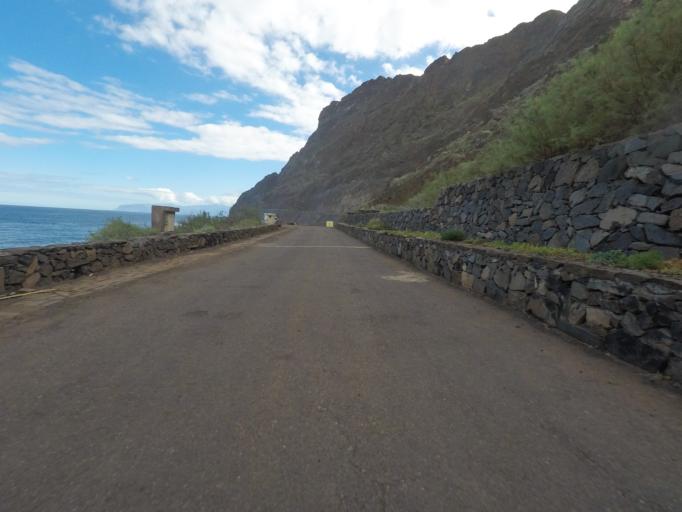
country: ES
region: Canary Islands
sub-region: Provincia de Santa Cruz de Tenerife
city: Hermigua
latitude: 28.1772
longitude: -17.1778
